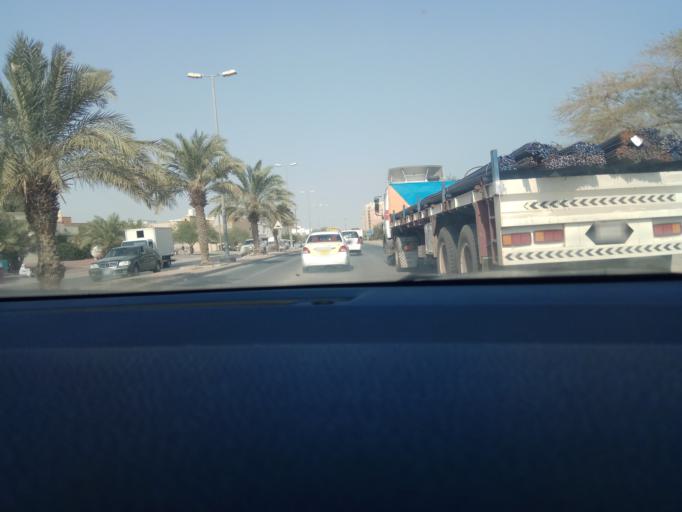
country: KW
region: Al Ahmadi
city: Al Fahahil
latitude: 29.0756
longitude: 48.1248
